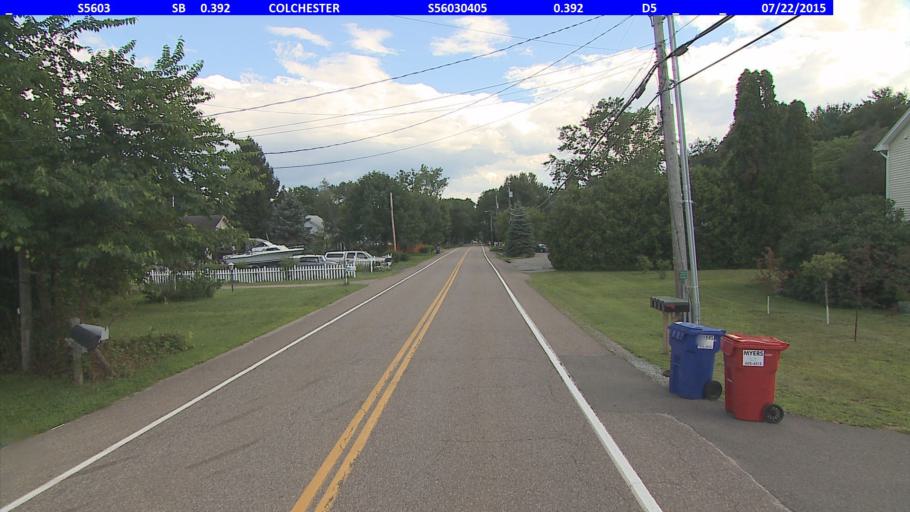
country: US
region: Vermont
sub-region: Chittenden County
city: Burlington
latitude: 44.5436
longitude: -73.2502
